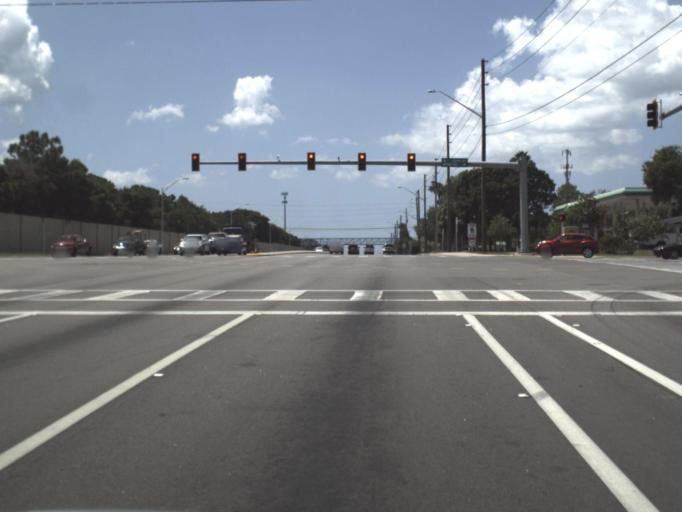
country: US
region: Florida
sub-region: Pinellas County
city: Ridgecrest
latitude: 27.8948
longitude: -82.7949
